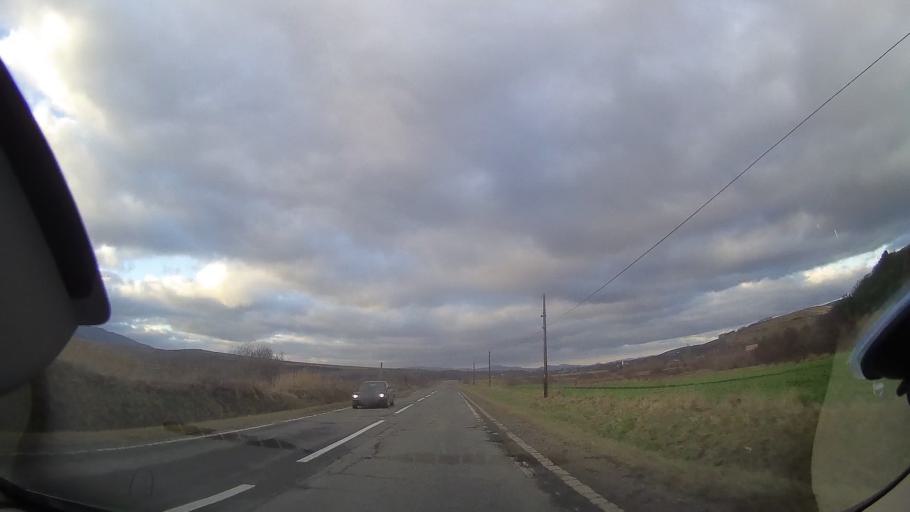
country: RO
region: Cluj
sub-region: Comuna Calatele
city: Calatele
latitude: 46.7881
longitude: 22.9994
